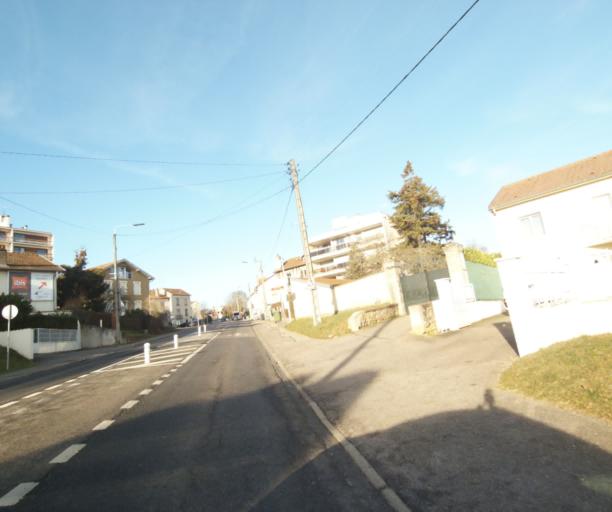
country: FR
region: Lorraine
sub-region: Departement de Meurthe-et-Moselle
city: Villers-les-Nancy
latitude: 48.6607
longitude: 6.1650
